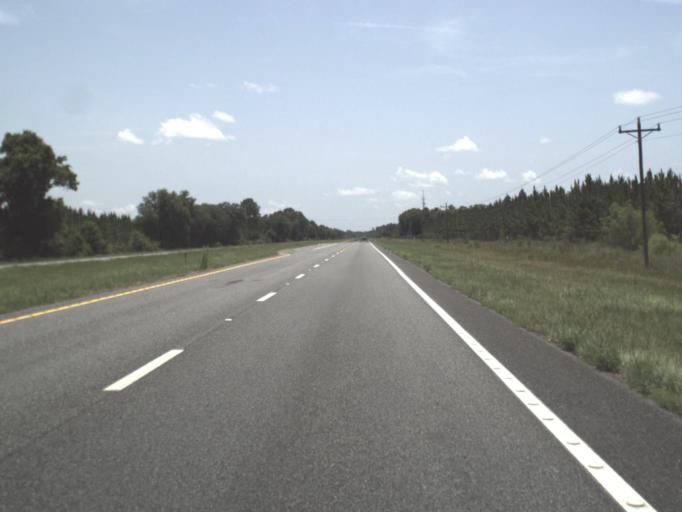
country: US
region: Florida
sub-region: Taylor County
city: Steinhatchee
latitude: 29.7946
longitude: -83.3355
